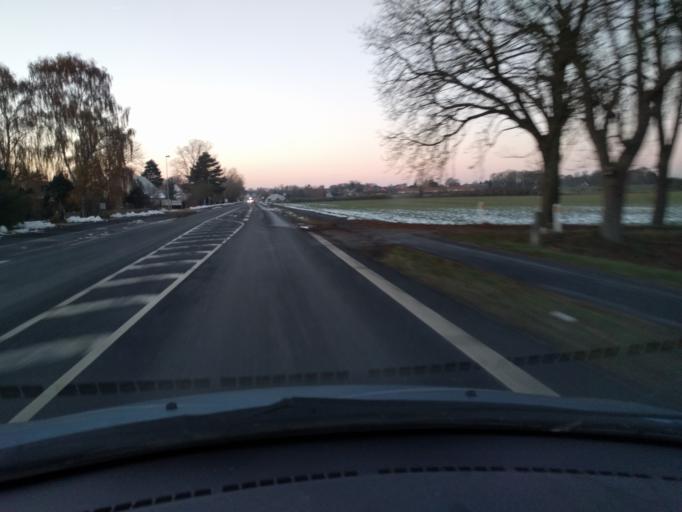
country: DK
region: South Denmark
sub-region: Nyborg Kommune
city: Nyborg
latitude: 55.3490
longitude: 10.7337
